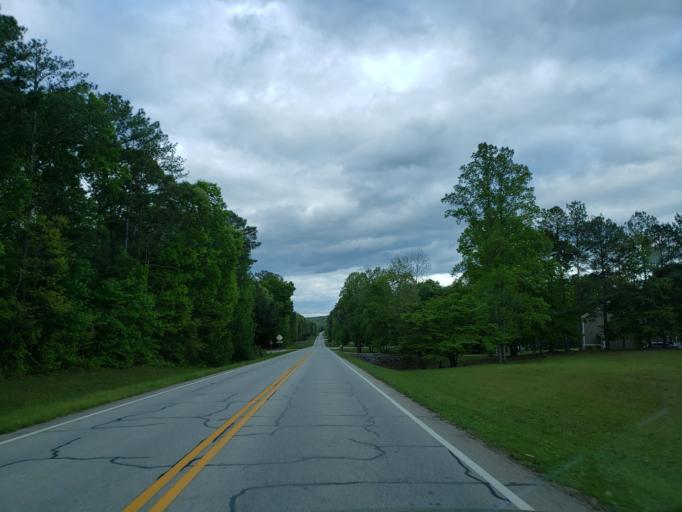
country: US
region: Georgia
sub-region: Carroll County
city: Temple
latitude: 33.8219
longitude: -85.0814
